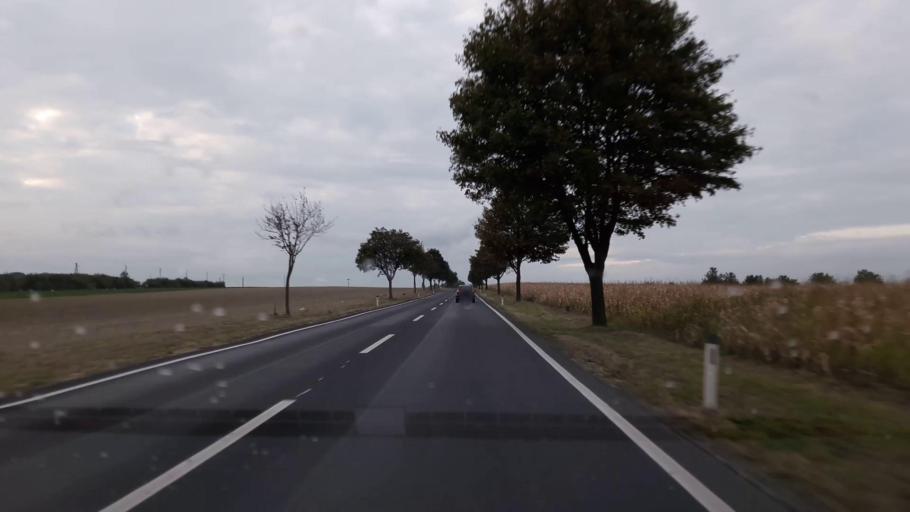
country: AT
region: Lower Austria
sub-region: Politischer Bezirk Wien-Umgebung
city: Schwadorf
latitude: 48.0779
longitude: 16.5729
